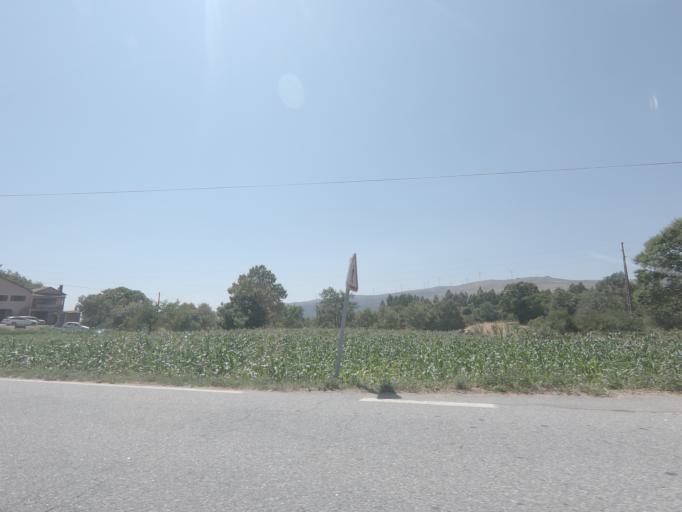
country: PT
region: Viseu
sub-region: Castro Daire
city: Castro Daire
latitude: 40.9639
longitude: -7.8848
